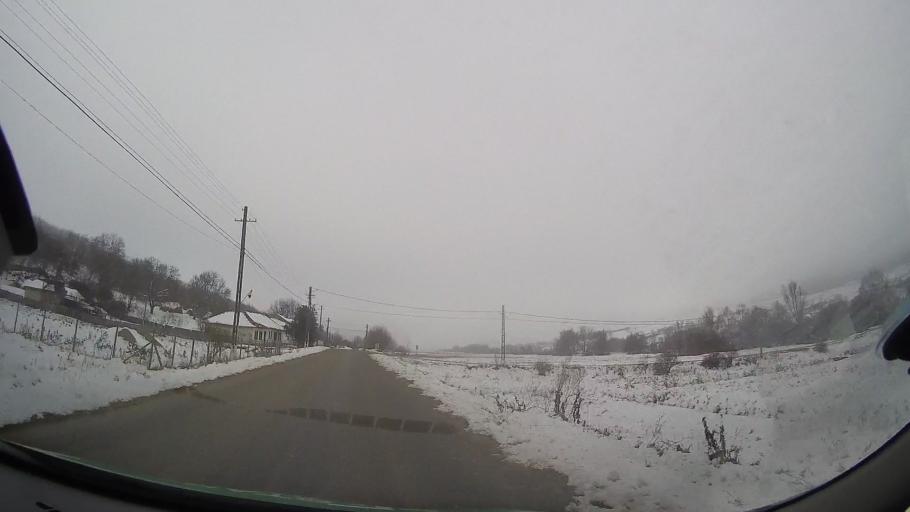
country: RO
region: Bacau
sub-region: Comuna Vultureni
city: Vultureni
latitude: 46.3272
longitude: 27.2916
